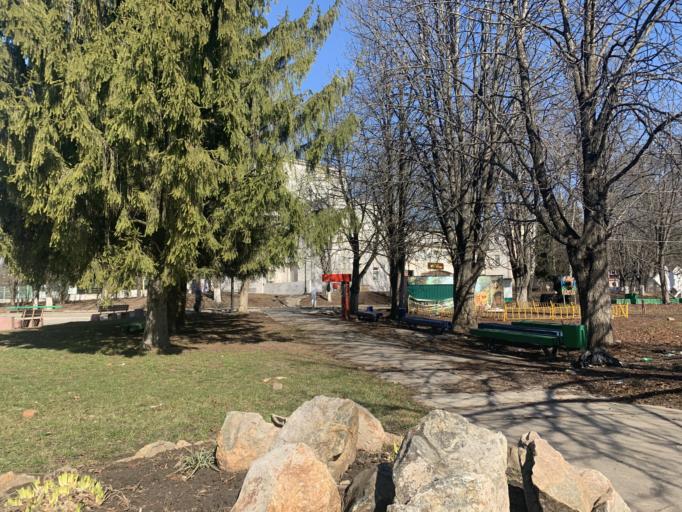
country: RU
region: Kursk
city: Zheleznogorsk
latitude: 52.3259
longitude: 35.3598
